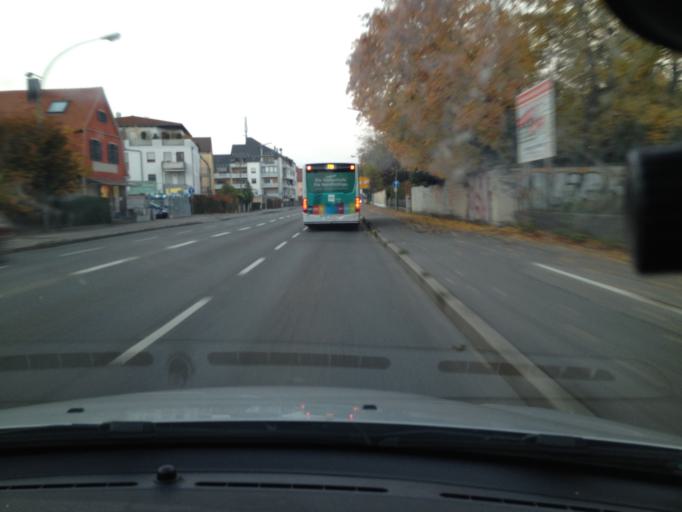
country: DE
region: Bavaria
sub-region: Swabia
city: Konigsbrunn
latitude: 48.3056
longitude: 10.9039
